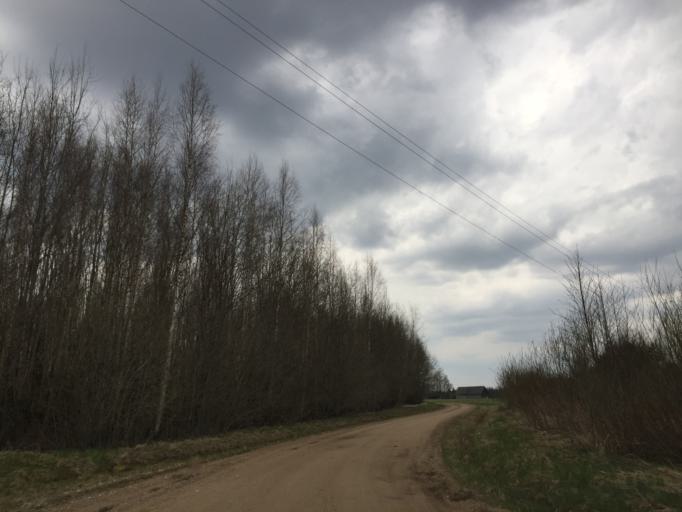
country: EE
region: Vorumaa
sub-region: Antsla vald
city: Vana-Antsla
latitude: 57.9443
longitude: 26.7183
